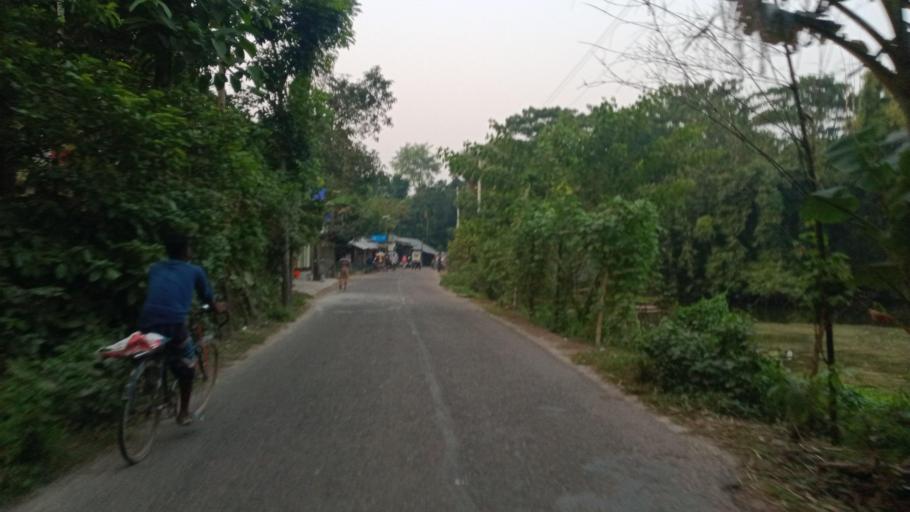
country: BD
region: Chittagong
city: Hajiganj
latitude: 23.3711
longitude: 90.9827
